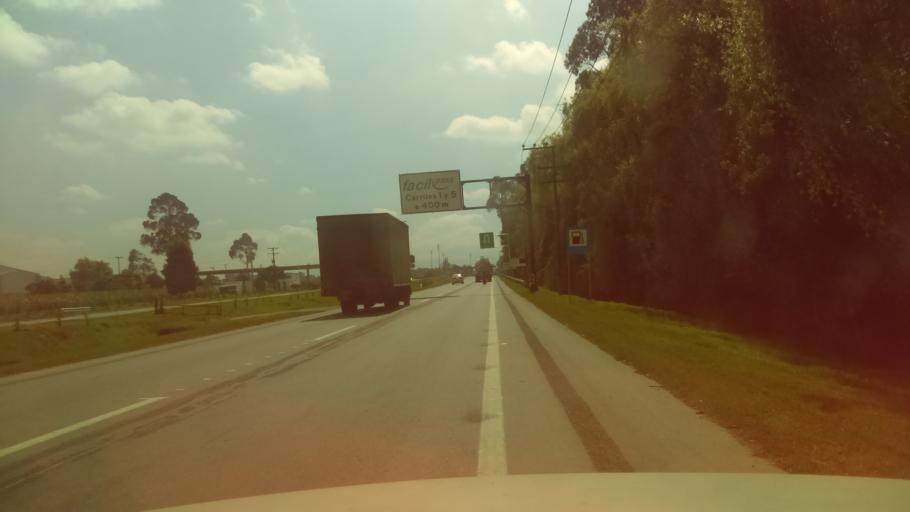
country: CO
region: Cundinamarca
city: Madrid
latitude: 4.7511
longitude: -74.2954
